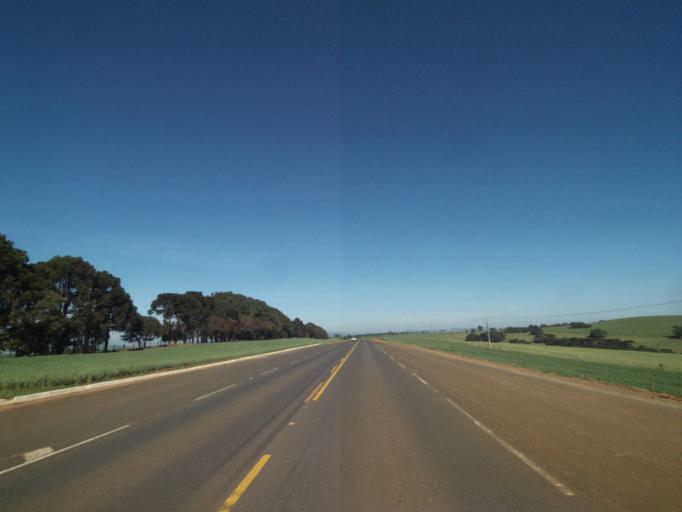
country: BR
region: Parana
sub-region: Tibagi
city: Tibagi
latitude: -24.4178
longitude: -50.3689
